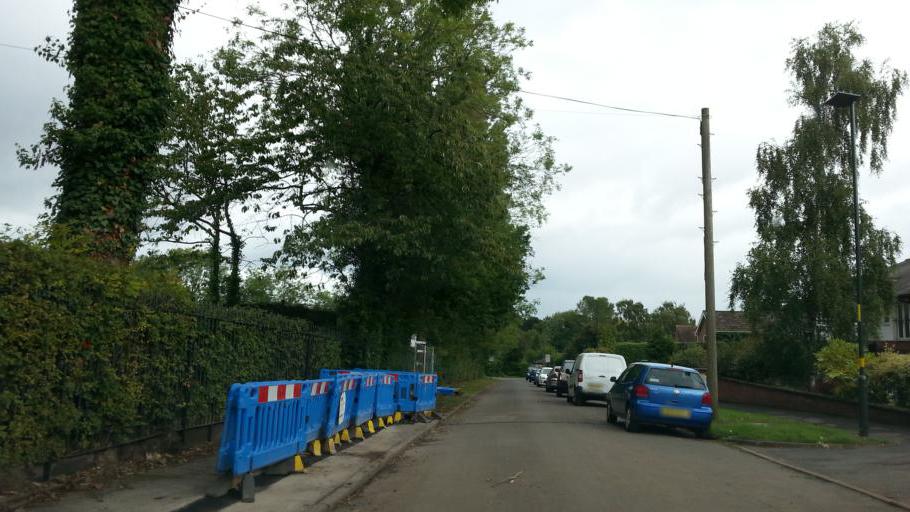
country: GB
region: England
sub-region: City and Borough of Birmingham
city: Birmingham
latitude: 52.4408
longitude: -1.9174
